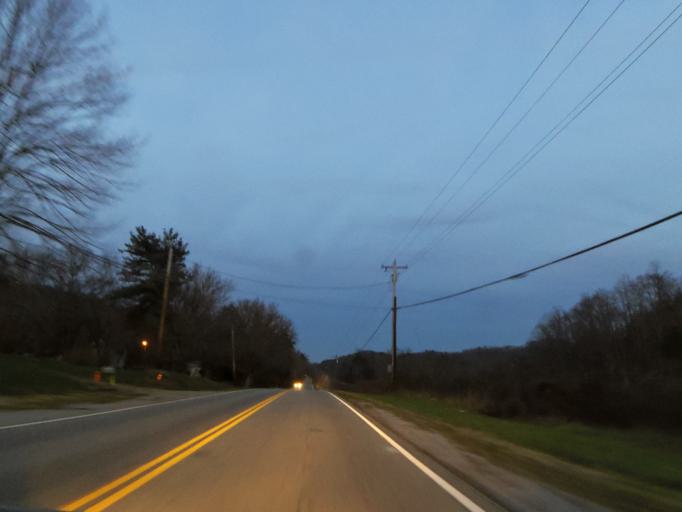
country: US
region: Tennessee
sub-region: Morgan County
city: Coalfield
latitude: 35.9964
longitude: -84.4129
